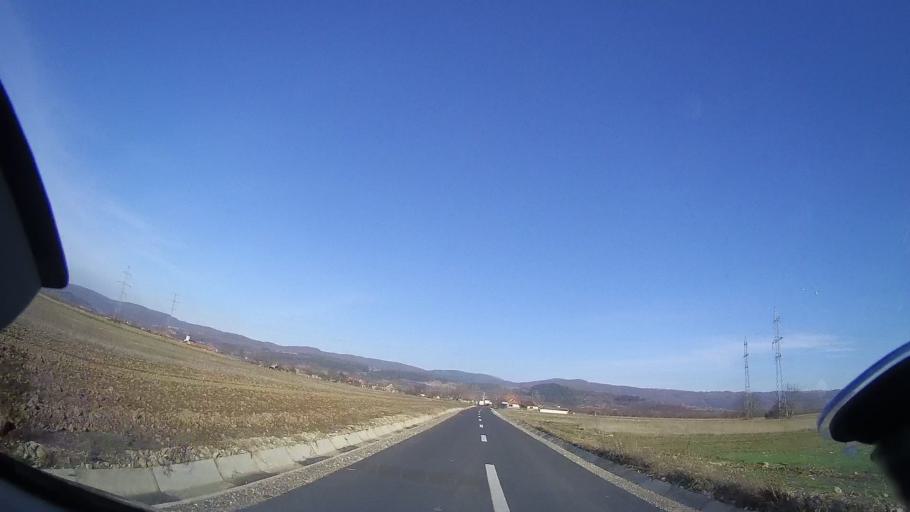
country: RO
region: Bihor
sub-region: Comuna Auseu
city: Auseu
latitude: 47.0172
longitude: 22.4917
